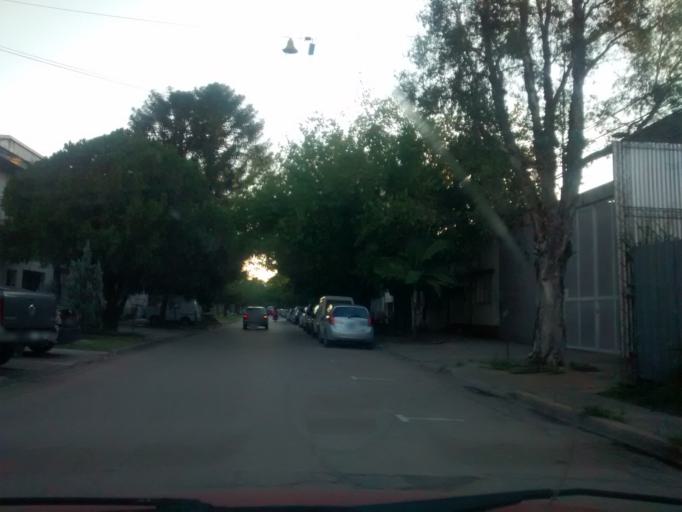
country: AR
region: Chaco
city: Resistencia
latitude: -27.4459
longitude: -58.9858
